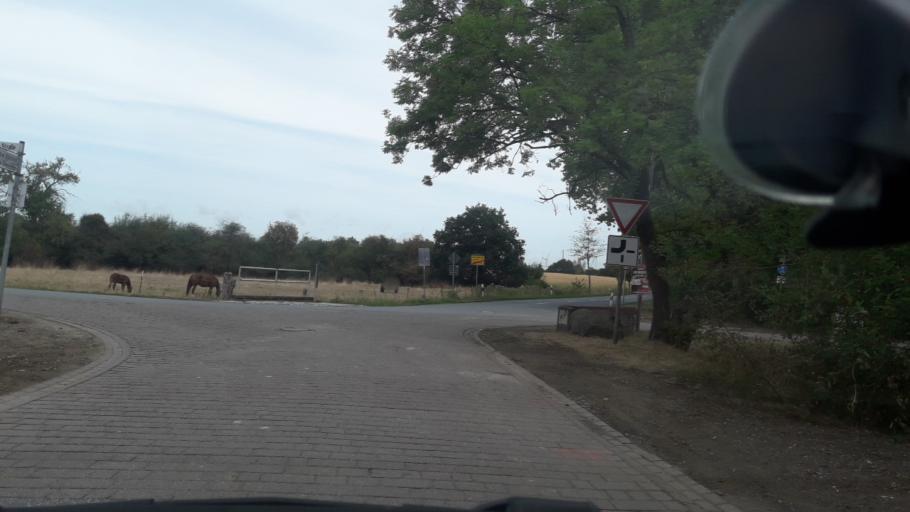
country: DE
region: Lower Saxony
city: Gross Twulpstedt
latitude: 52.3456
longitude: 10.8589
